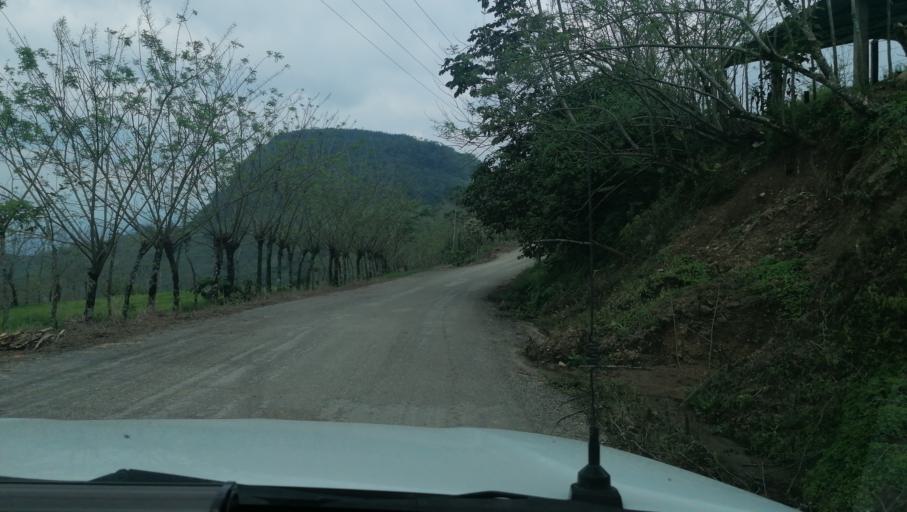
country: MX
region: Chiapas
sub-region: Francisco Leon
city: San Miguel la Sardina
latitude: 17.2707
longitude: -93.2648
